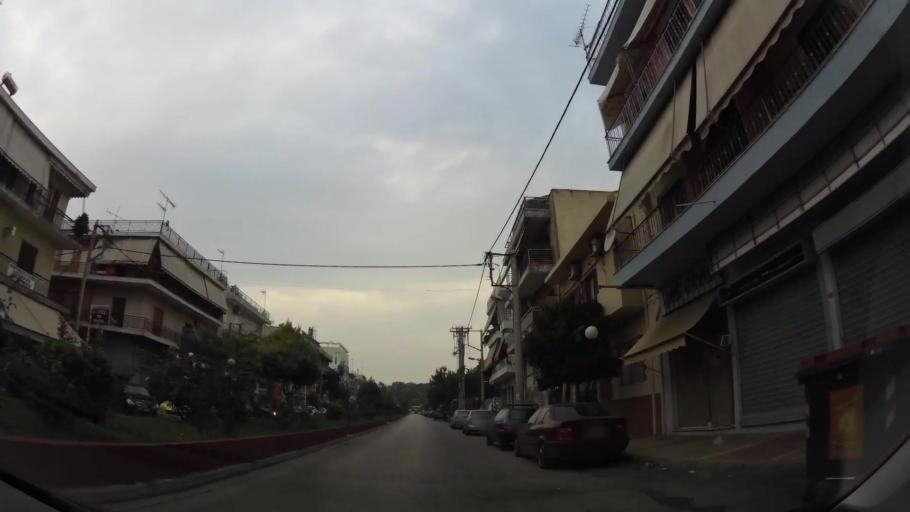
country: GR
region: Attica
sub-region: Nomarchia Athinas
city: Peristeri
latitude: 38.0033
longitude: 23.6902
